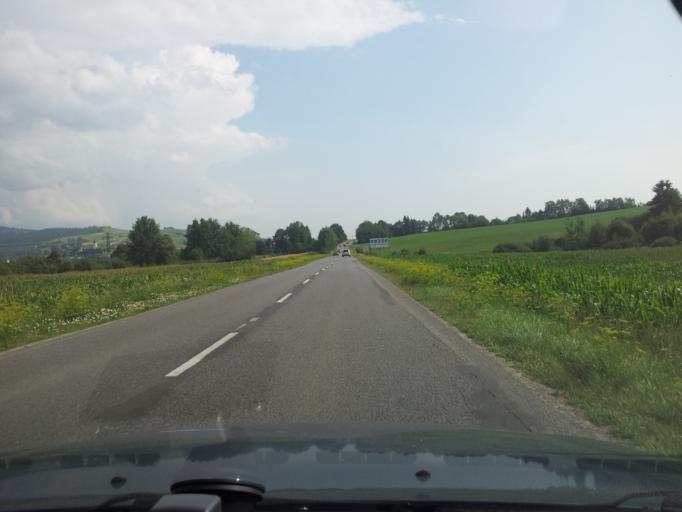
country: SK
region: Zilinsky
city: Namestovo
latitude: 49.3780
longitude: 19.4301
